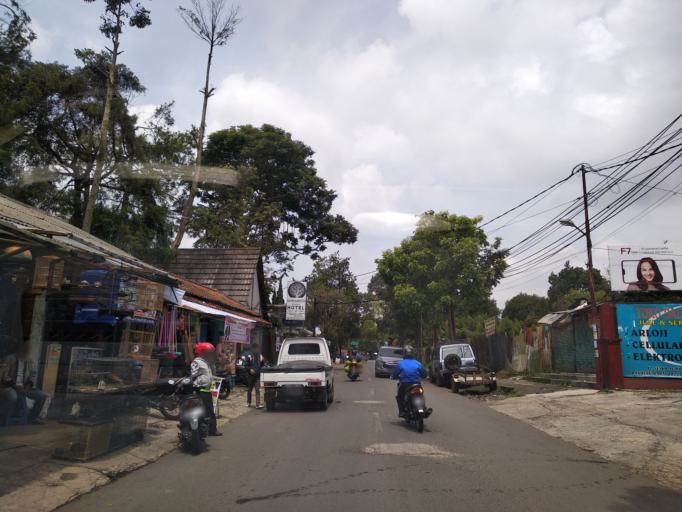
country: ID
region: West Java
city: Lembang
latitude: -6.8162
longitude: 107.6254
